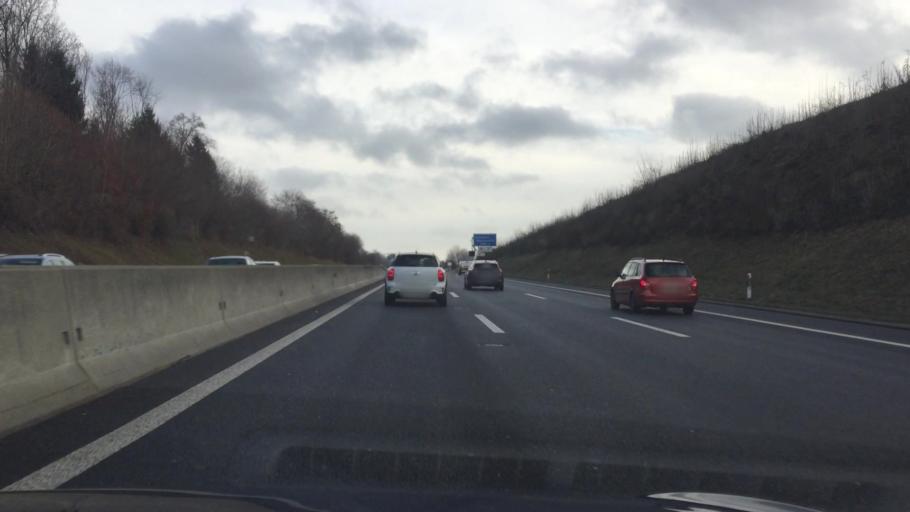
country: CH
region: Vaud
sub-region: Lausanne District
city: Romanel
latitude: 46.5534
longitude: 6.6070
